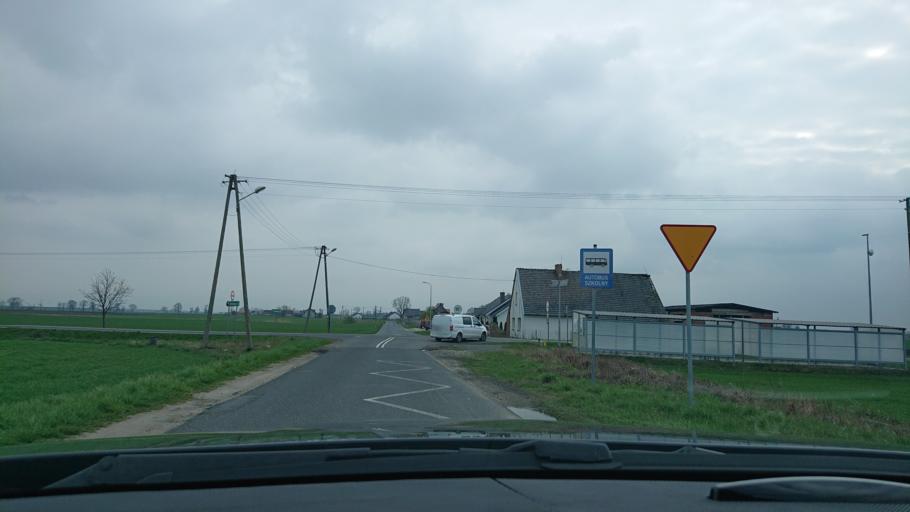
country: PL
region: Greater Poland Voivodeship
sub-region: Powiat gnieznienski
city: Lubowo
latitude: 52.5427
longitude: 17.4946
